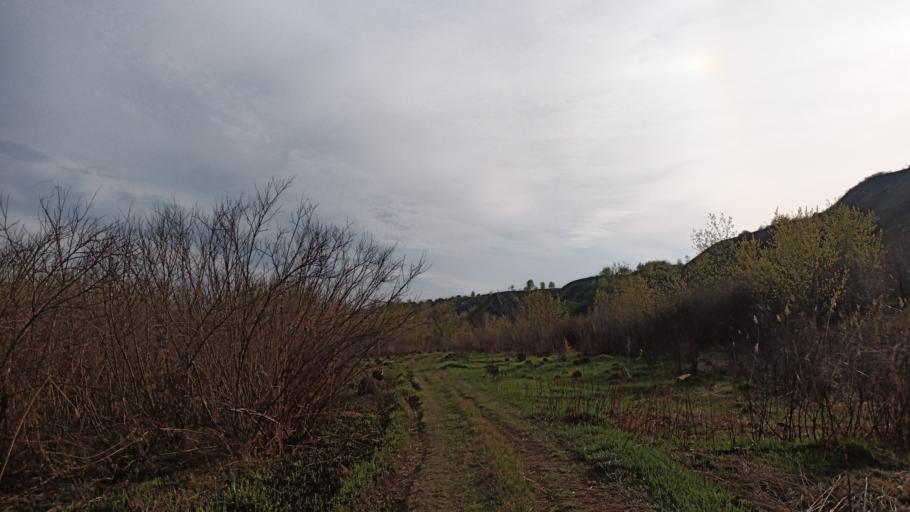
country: RU
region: Altai Krai
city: Yuzhnyy
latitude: 53.2235
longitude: 83.7277
